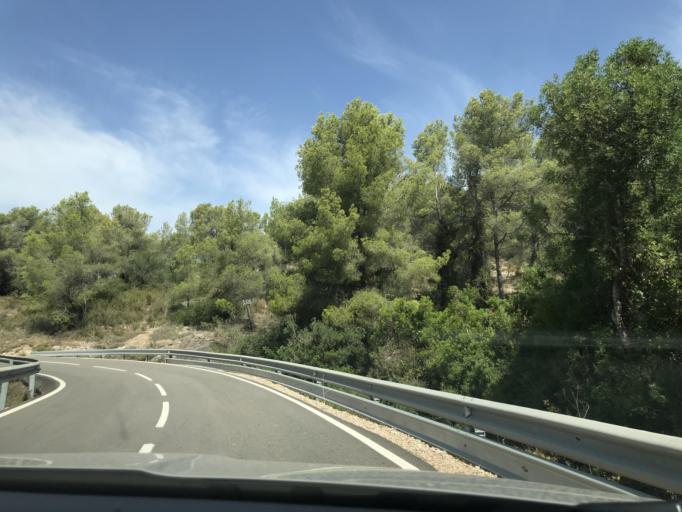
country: ES
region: Catalonia
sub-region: Provincia de Tarragona
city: Salomo
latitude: 41.2079
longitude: 1.3891
